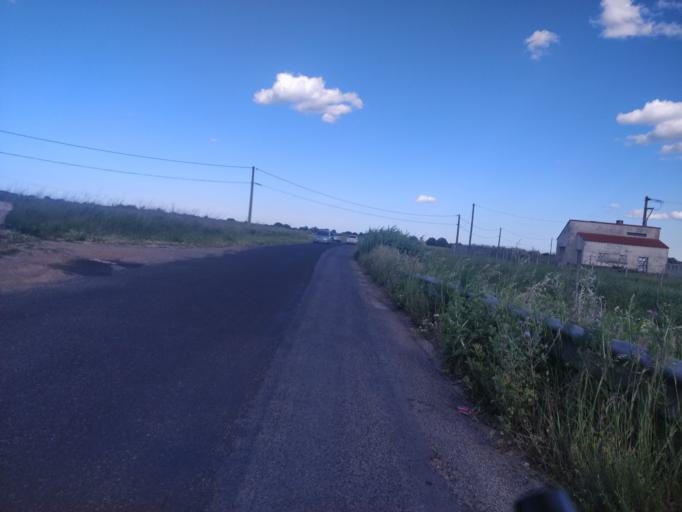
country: FR
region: Languedoc-Roussillon
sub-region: Departement des Pyrenees-Orientales
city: Cabestany
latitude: 42.6730
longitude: 2.9244
